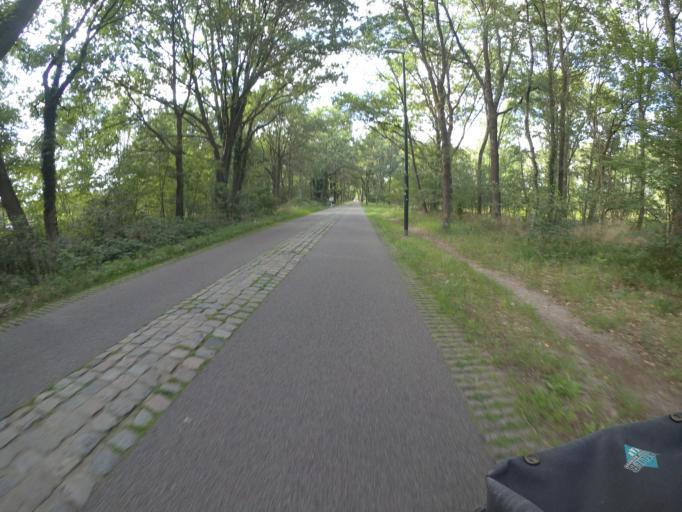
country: NL
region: North Brabant
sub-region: Gemeente Eindhoven
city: Eindhoven
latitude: 51.4101
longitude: 5.4718
